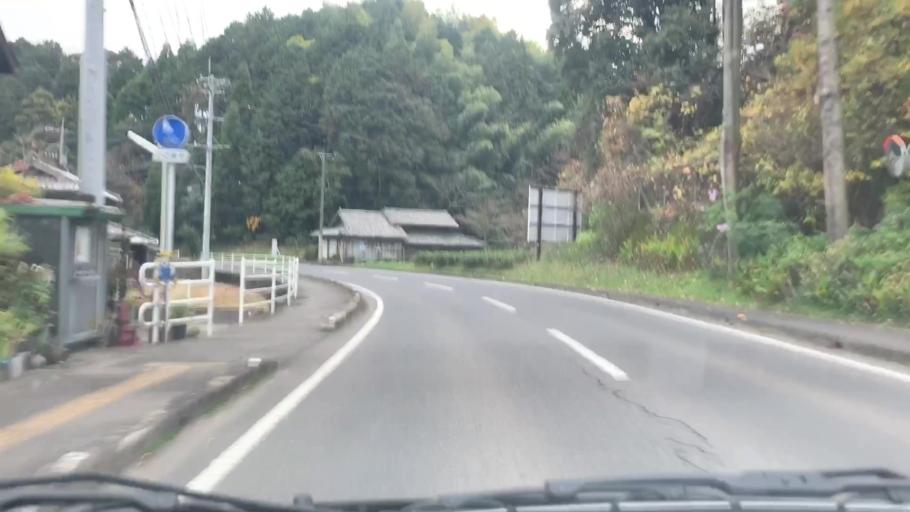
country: JP
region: Saga Prefecture
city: Takeocho-takeo
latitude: 33.1918
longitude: 130.0321
